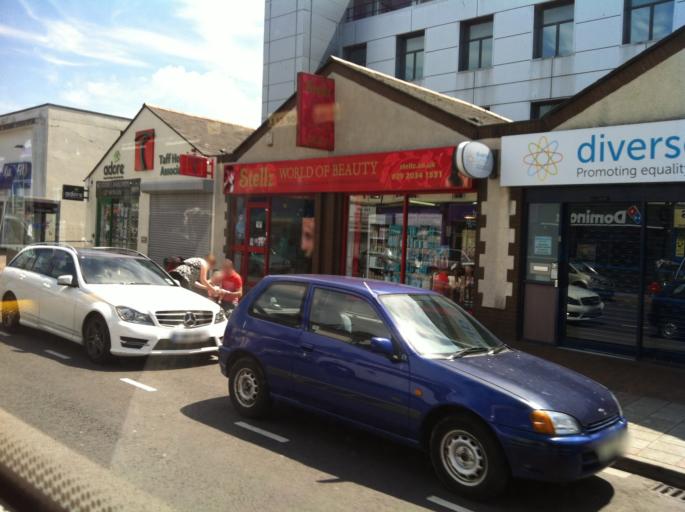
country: GB
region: Wales
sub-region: Cardiff
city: Cardiff
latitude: 51.4818
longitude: -3.2045
